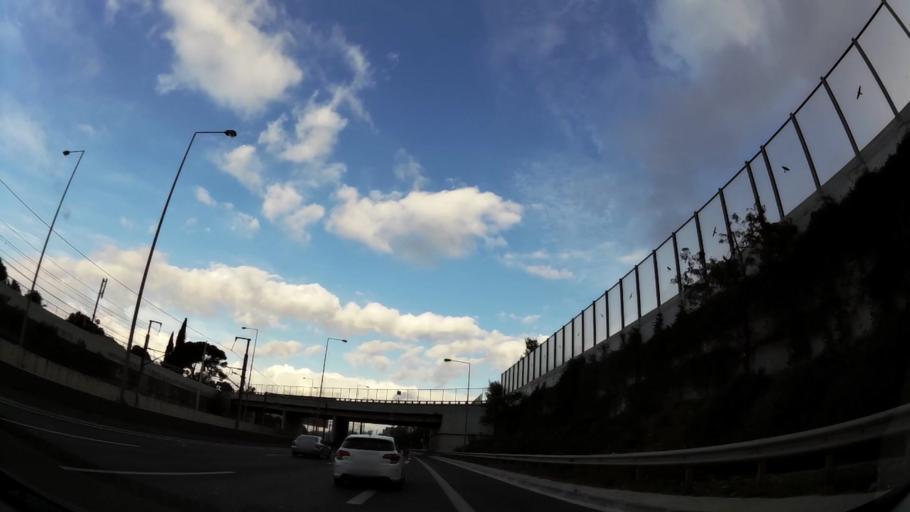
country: GR
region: Attica
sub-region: Nomarchia Athinas
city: Vrilissia
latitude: 38.0376
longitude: 23.8172
